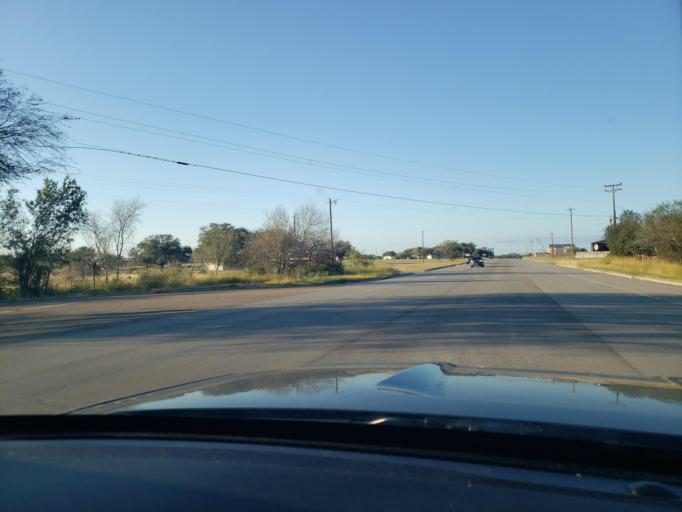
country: US
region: Texas
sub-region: Bee County
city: Beeville
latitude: 28.4167
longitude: -97.7214
